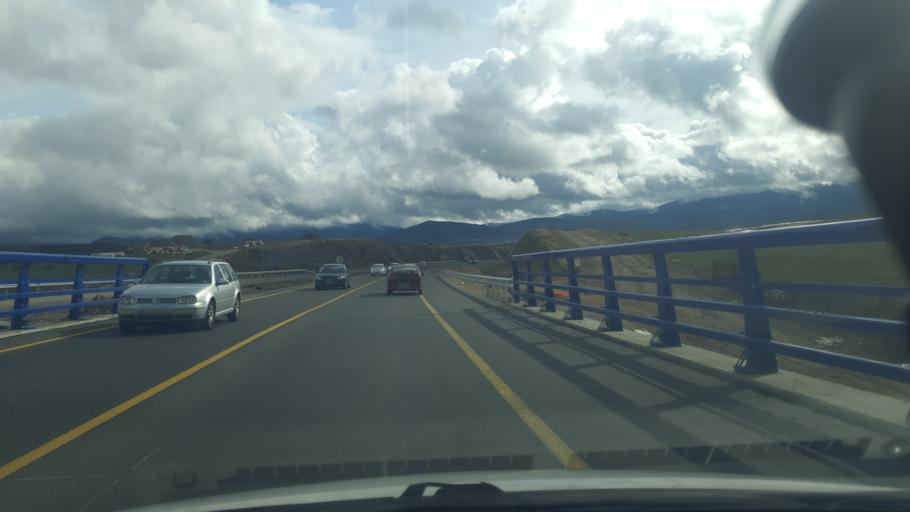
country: ES
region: Castille and Leon
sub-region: Provincia de Segovia
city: San Cristobal de Segovia
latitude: 40.9464
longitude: -4.0876
